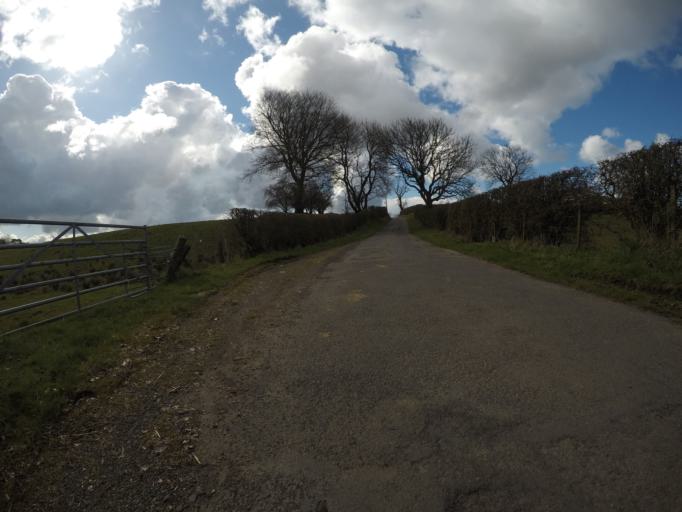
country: GB
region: Scotland
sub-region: North Ayrshire
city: Kilbirnie
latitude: 55.7235
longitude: -4.6660
